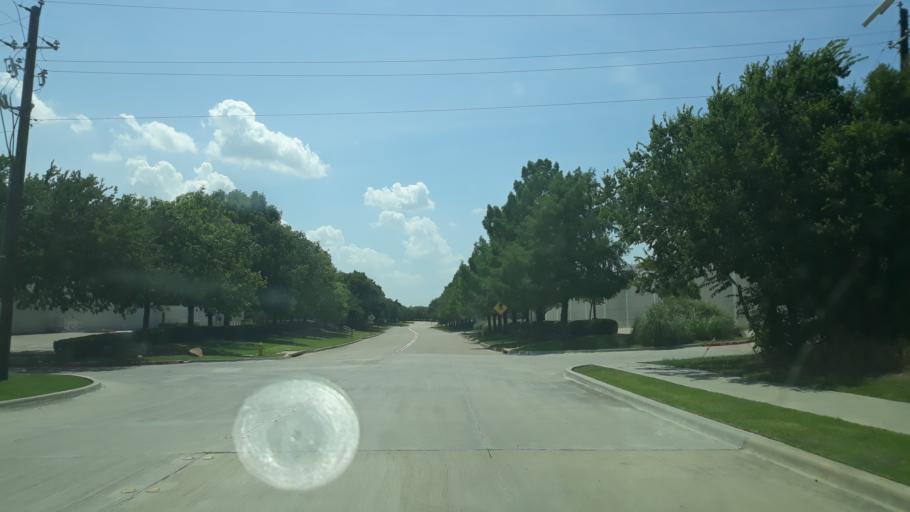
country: US
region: Texas
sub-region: Dallas County
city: Coppell
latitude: 32.9610
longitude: -97.0237
